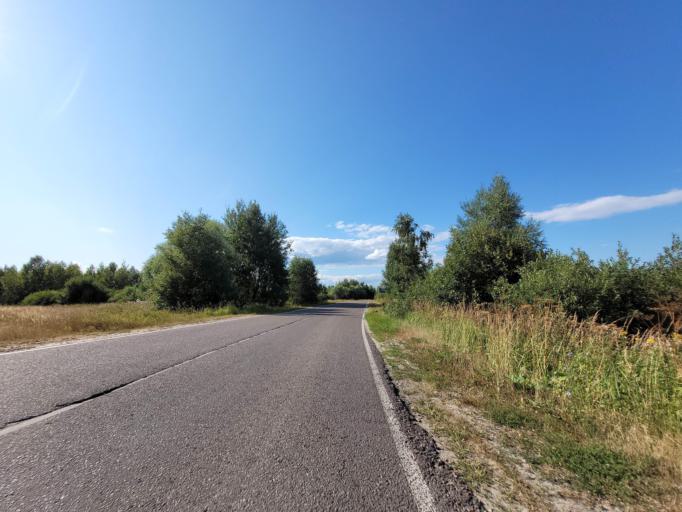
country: RU
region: Moskovskaya
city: Konobeyevo
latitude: 55.4011
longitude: 38.7097
